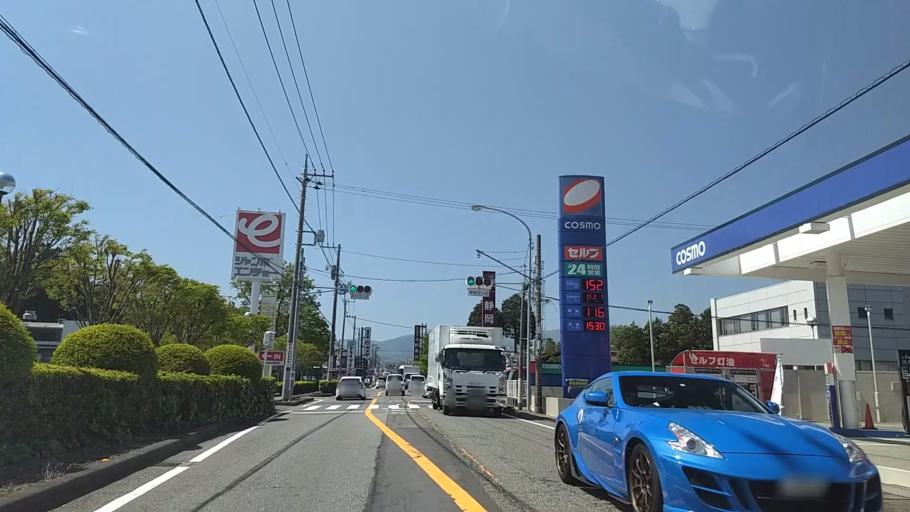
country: JP
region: Shizuoka
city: Gotemba
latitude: 35.2976
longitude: 138.9421
